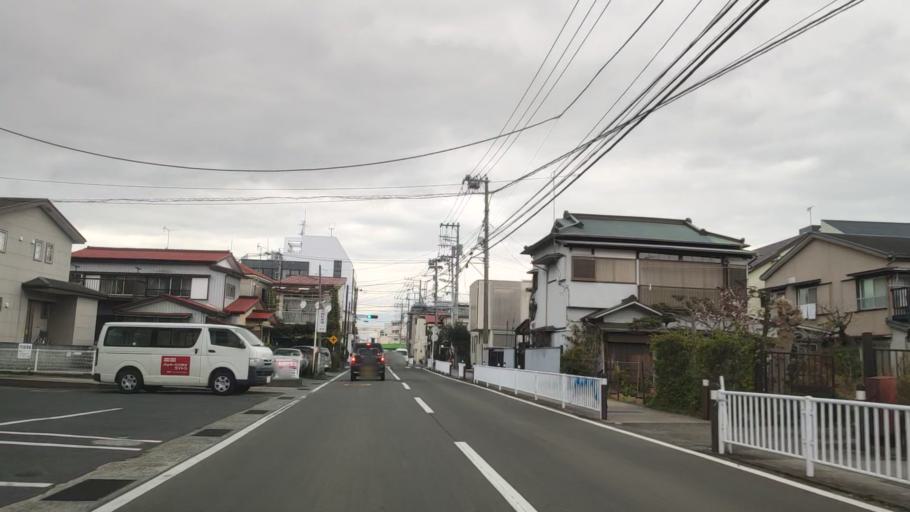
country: JP
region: Kanagawa
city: Odawara
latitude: 35.2596
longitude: 139.1631
